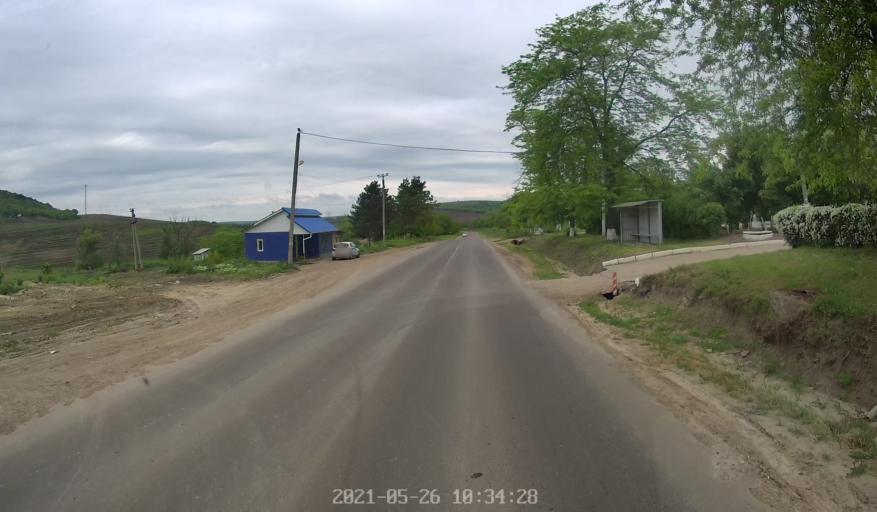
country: MD
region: Hincesti
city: Hincesti
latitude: 46.8747
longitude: 28.4732
